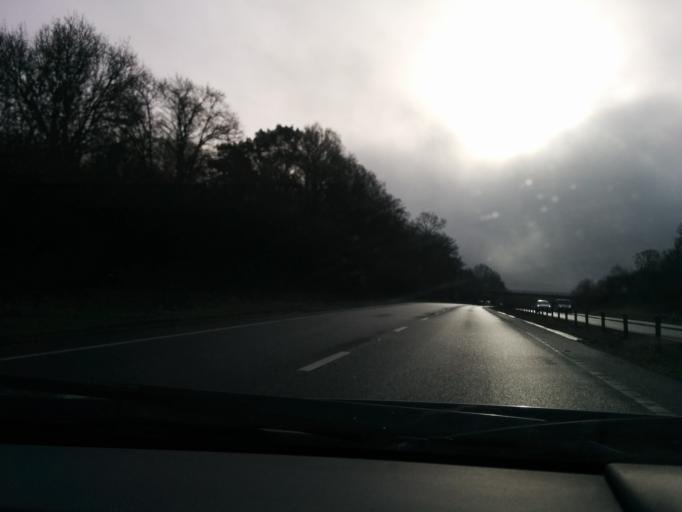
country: GB
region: England
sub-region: Hampshire
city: Highclere
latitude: 51.3787
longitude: -1.3632
